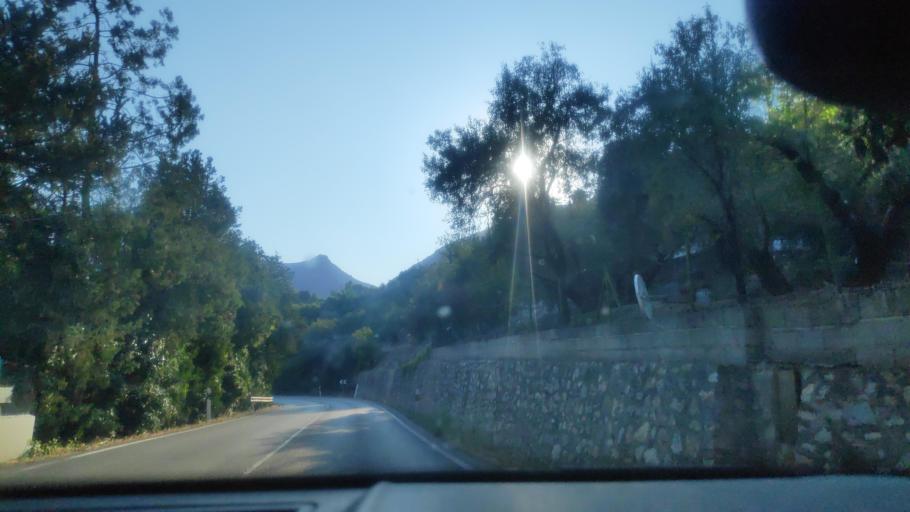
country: ES
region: Andalusia
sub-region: Provincia de Jaen
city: Jaen
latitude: 37.7506
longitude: -3.7932
